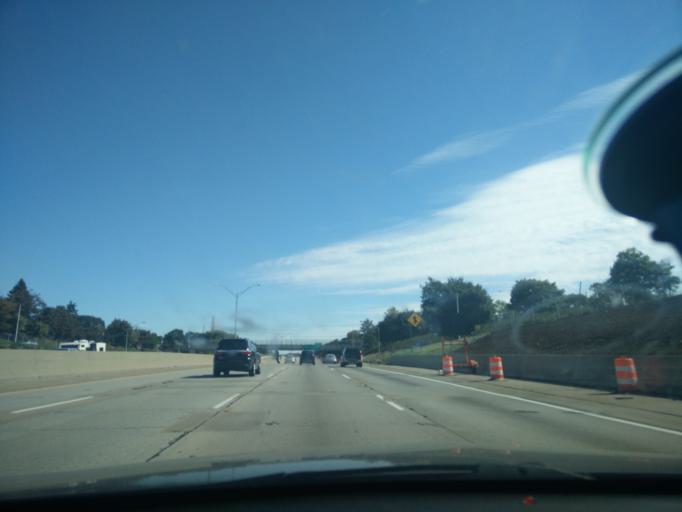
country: US
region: Michigan
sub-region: Macomb County
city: Center Line
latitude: 42.4920
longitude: -83.0043
